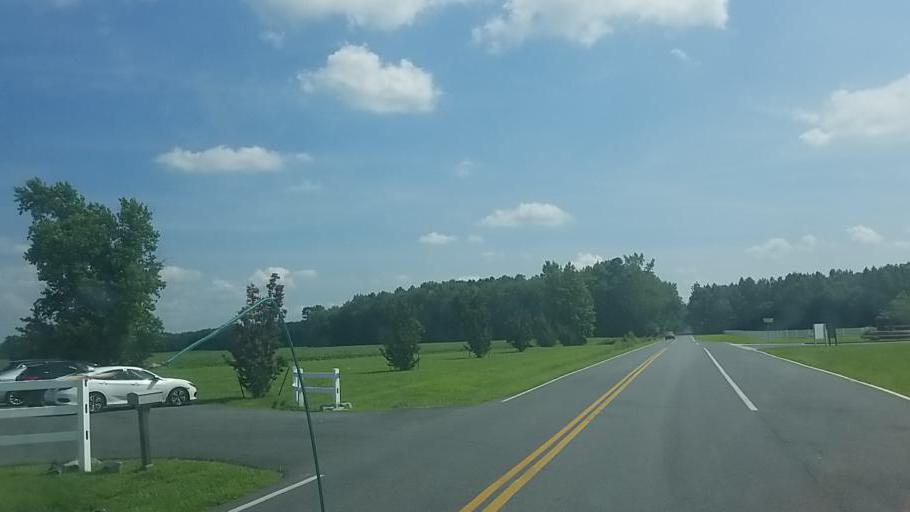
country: US
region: Maryland
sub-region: Wicomico County
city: Hebron
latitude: 38.4461
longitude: -75.6986
